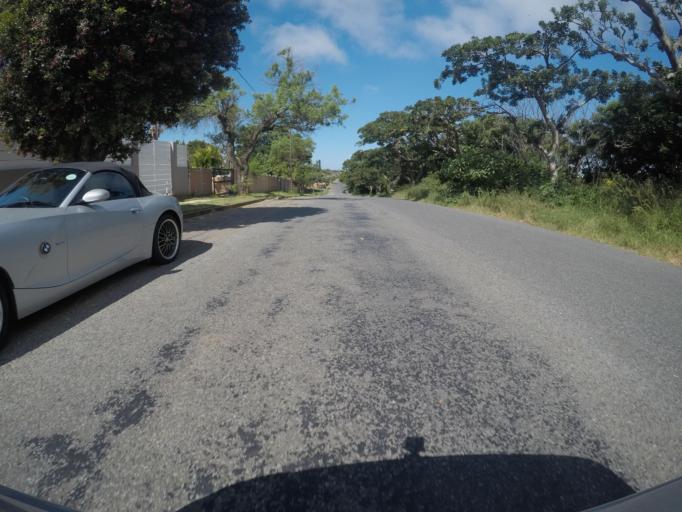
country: ZA
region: Eastern Cape
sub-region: Buffalo City Metropolitan Municipality
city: East London
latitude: -32.9833
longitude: 27.8873
